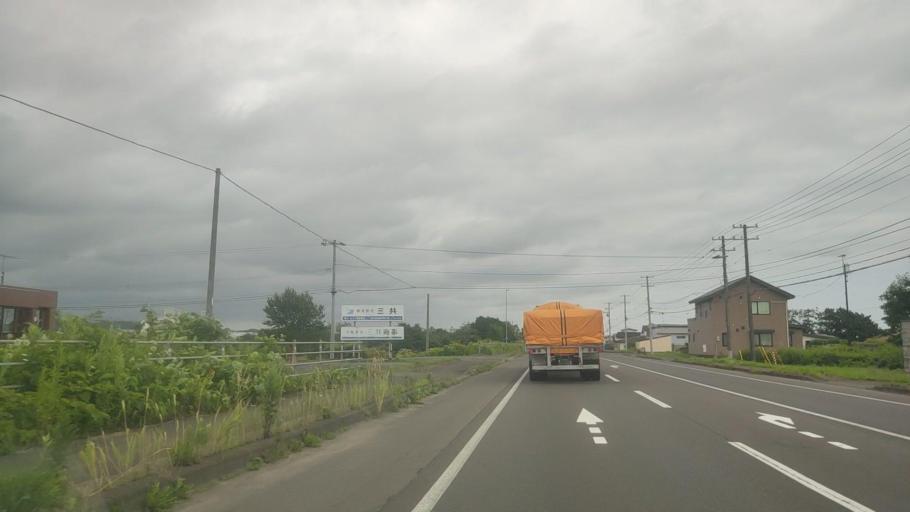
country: JP
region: Hokkaido
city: Shiraoi
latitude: 42.5224
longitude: 141.3113
